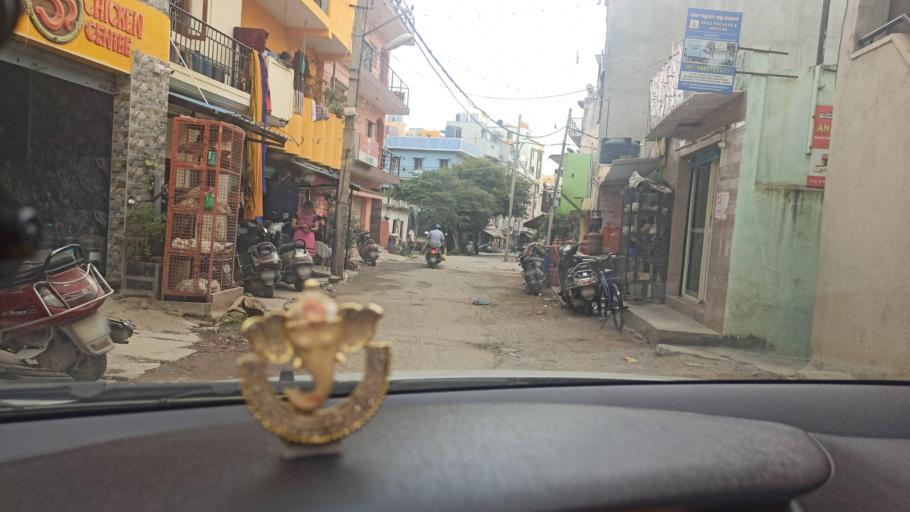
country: IN
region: Karnataka
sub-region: Bangalore Urban
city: Bangalore
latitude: 12.9106
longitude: 77.6281
